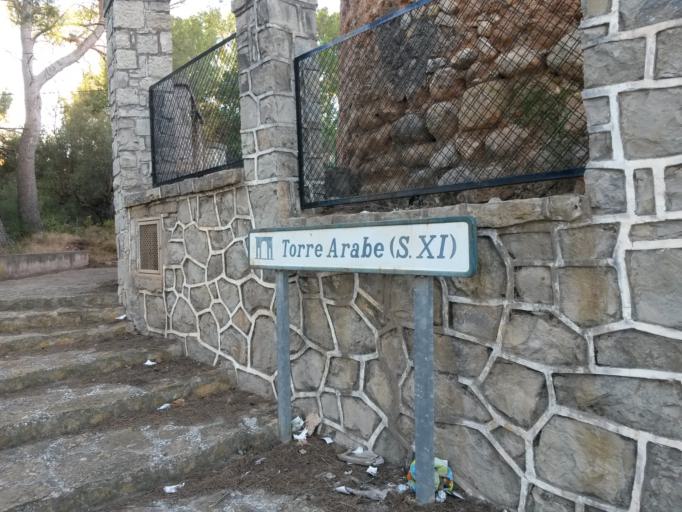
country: ES
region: Valencia
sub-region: Provincia de Castello
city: Navajas
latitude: 39.8731
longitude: -0.5090
